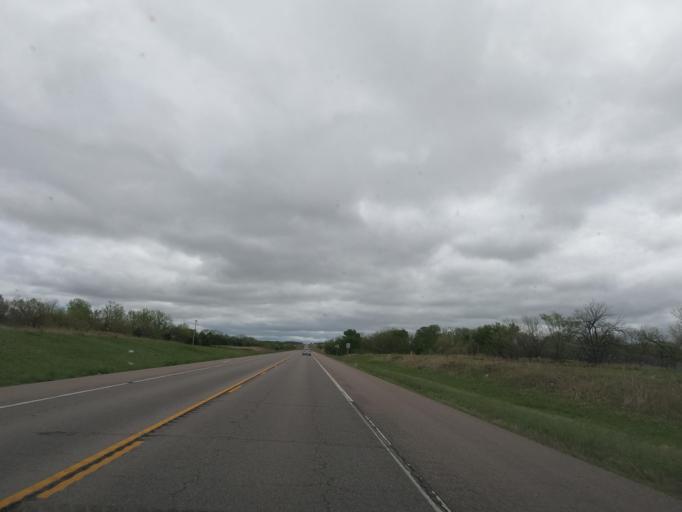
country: US
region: Kansas
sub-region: Elk County
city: Howard
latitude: 37.6367
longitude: -96.3642
